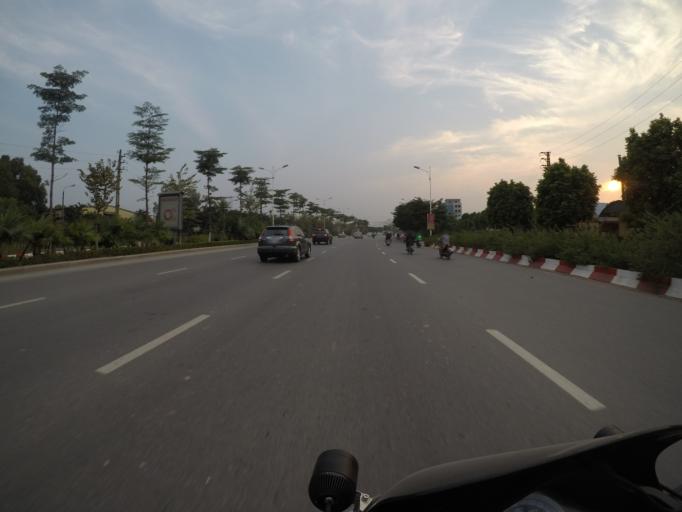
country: VN
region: Ha Noi
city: Trau Quy
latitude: 21.0333
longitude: 105.9012
